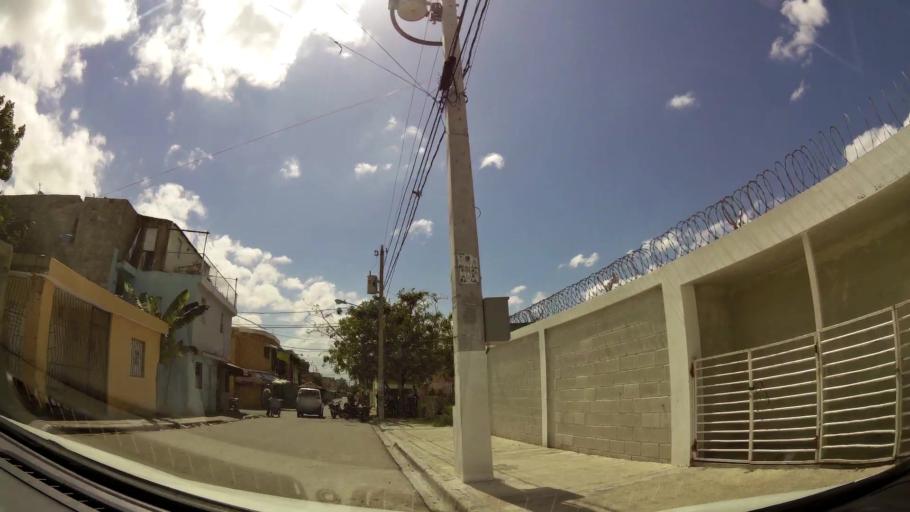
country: DO
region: San Cristobal
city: San Cristobal
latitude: 18.4286
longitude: -70.1163
